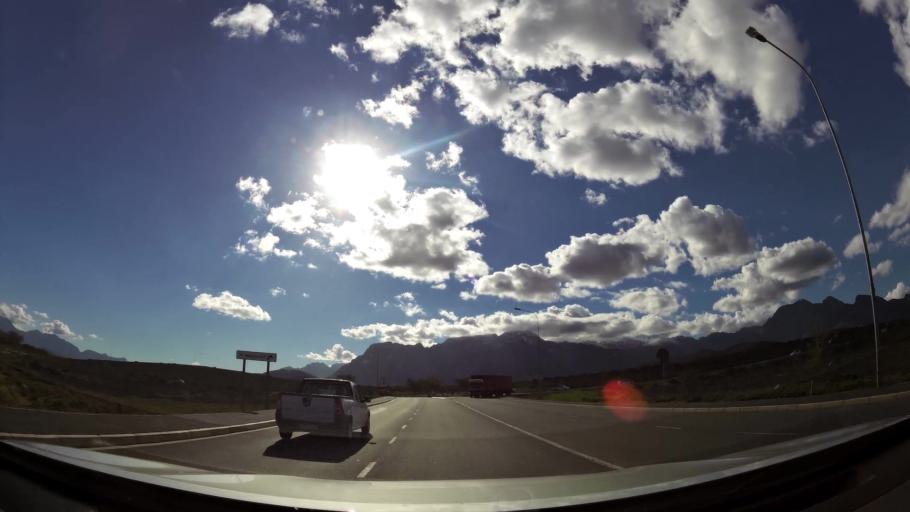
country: ZA
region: Western Cape
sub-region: Cape Winelands District Municipality
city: Worcester
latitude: -33.6354
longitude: 19.4283
